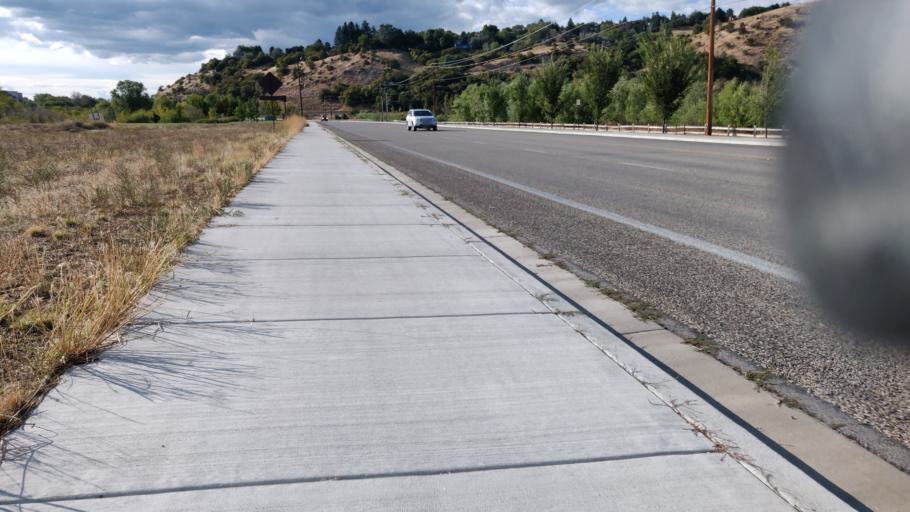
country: US
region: Idaho
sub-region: Ada County
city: Boise
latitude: 43.5772
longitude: -116.1419
